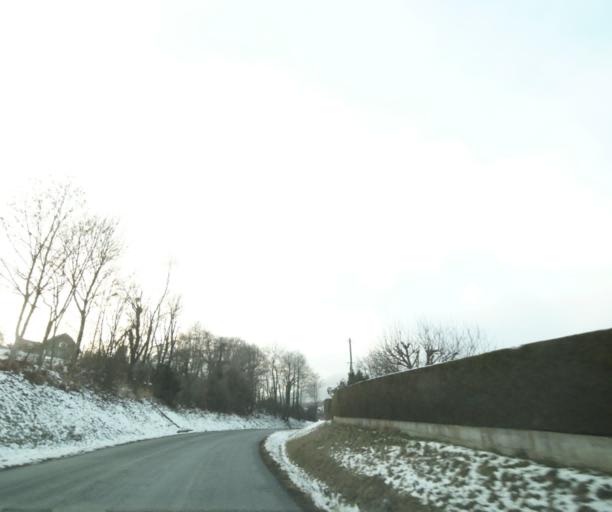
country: FR
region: Rhone-Alpes
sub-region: Departement de la Haute-Savoie
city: Vetraz-Monthoux
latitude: 46.1567
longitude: 6.2394
